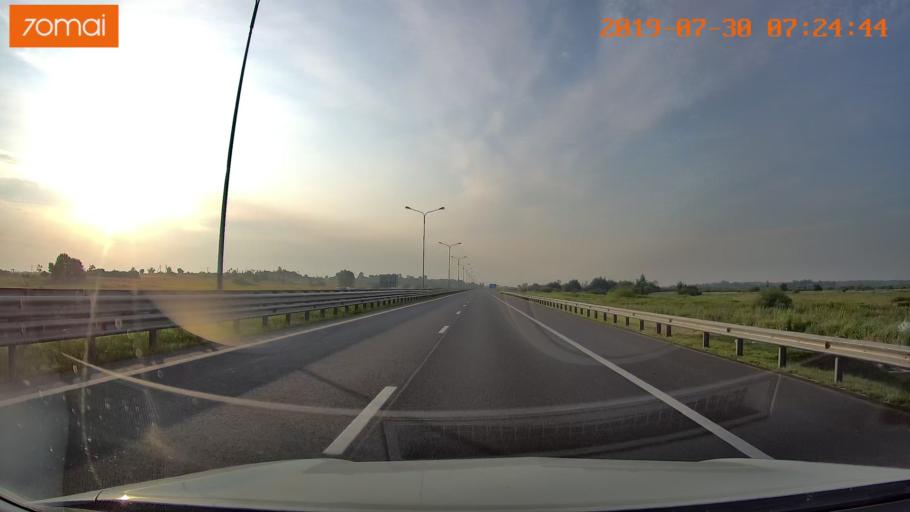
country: RU
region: Kaliningrad
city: Bol'shoe Isakovo
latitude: 54.6909
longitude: 20.8194
